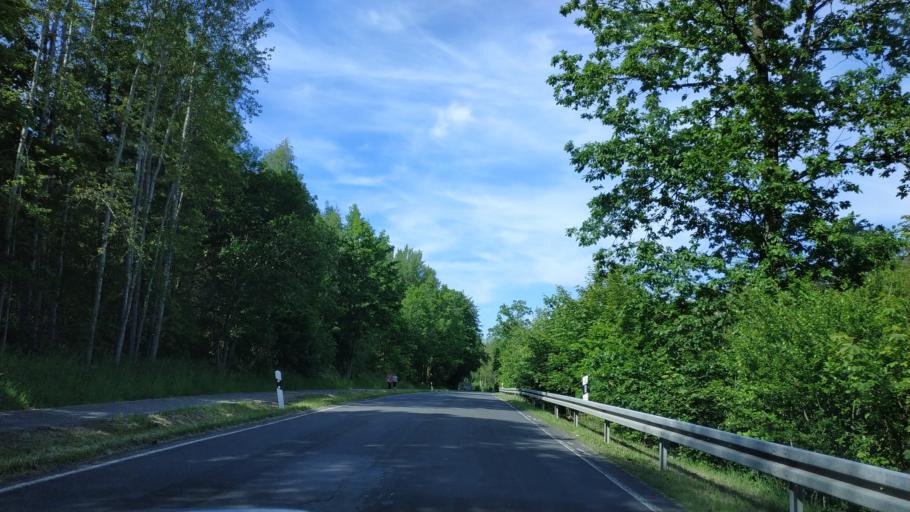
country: DE
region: Saxony
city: Plauen
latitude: 50.5270
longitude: 12.1336
